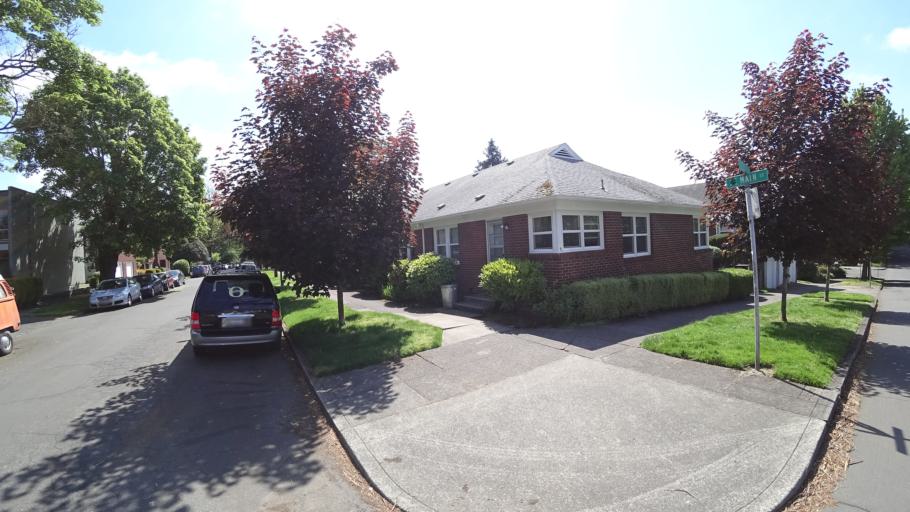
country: US
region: Oregon
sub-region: Multnomah County
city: Portland
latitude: 45.5135
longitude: -122.6391
